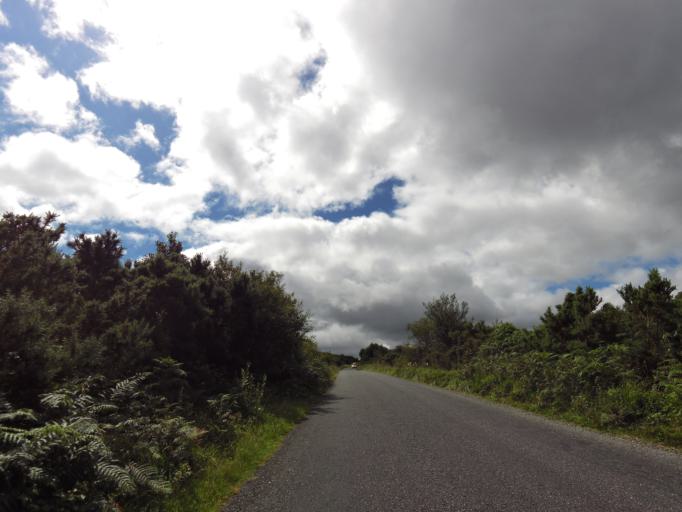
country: IE
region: Connaught
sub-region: County Galway
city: Oughterard
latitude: 53.4069
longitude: -9.3293
